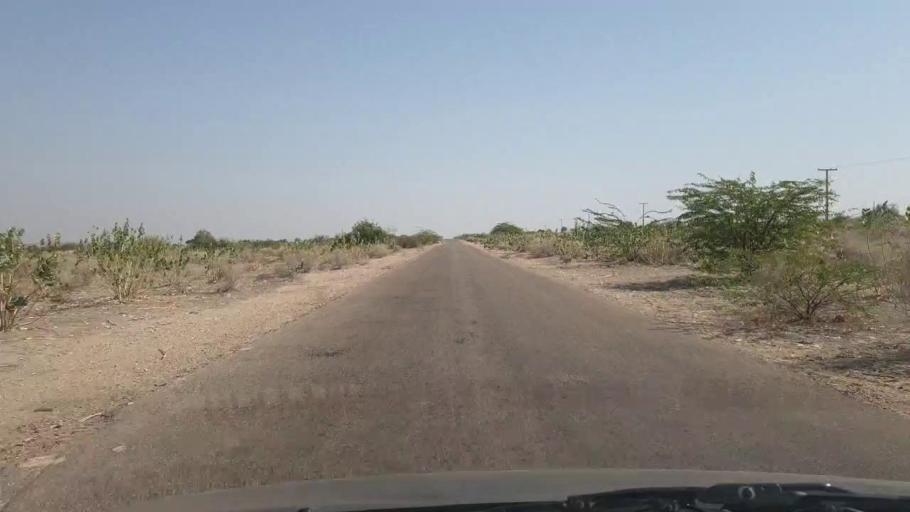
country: PK
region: Sindh
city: Chor
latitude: 25.5486
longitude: 69.8717
